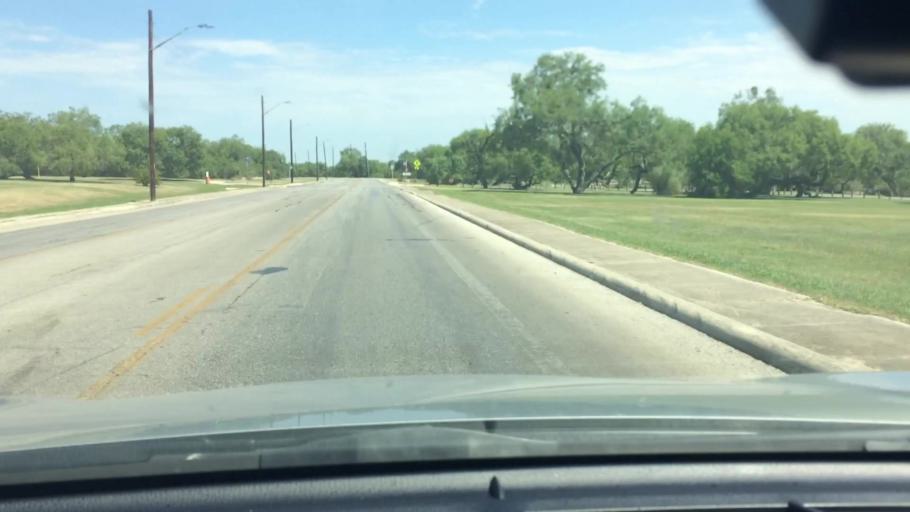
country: US
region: Texas
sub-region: Bexar County
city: San Antonio
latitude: 29.3840
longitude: -98.4306
